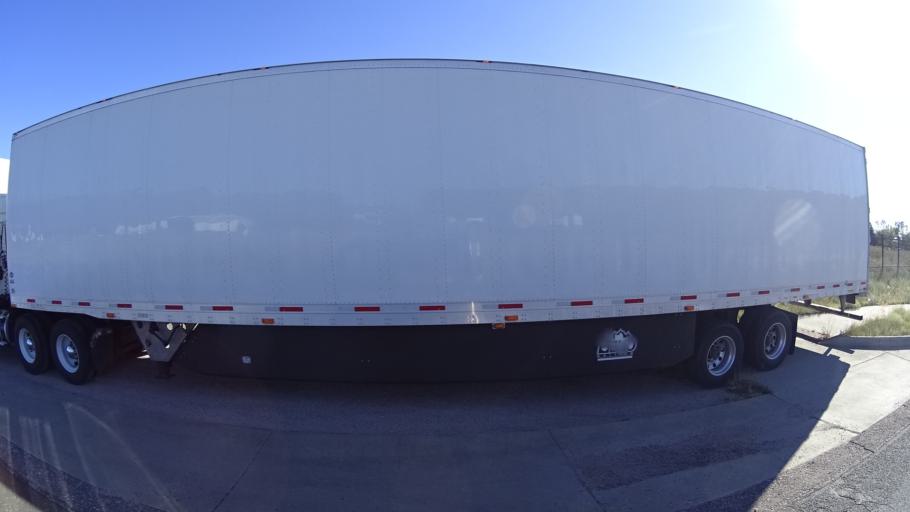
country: US
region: Colorado
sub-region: El Paso County
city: Cimarron Hills
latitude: 38.8150
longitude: -104.7269
